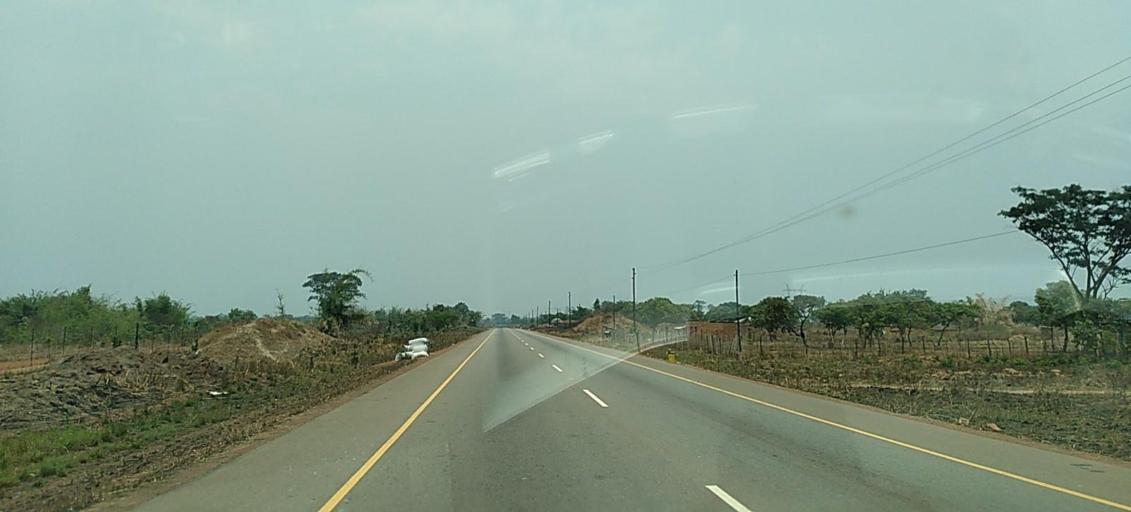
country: ZM
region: Copperbelt
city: Chililabombwe
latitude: -12.5383
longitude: 27.6064
